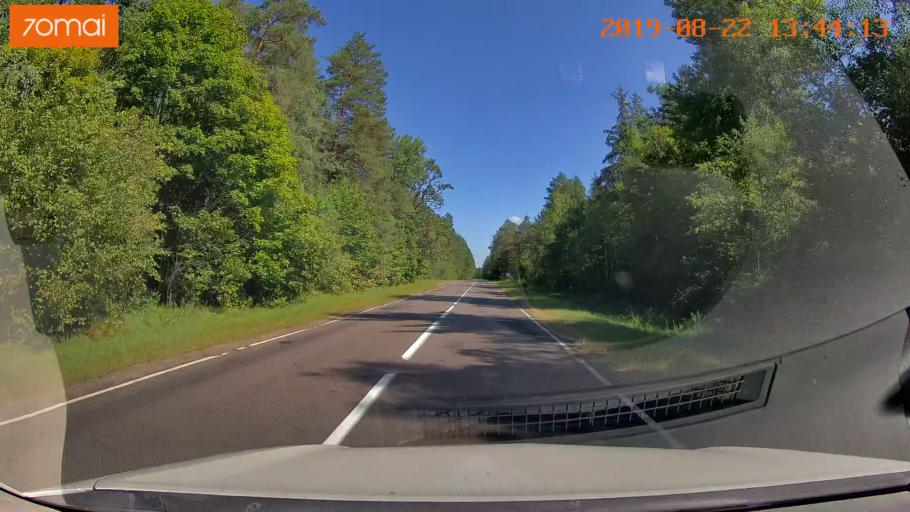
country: BY
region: Mogilev
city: Asipovichy
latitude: 53.2439
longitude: 28.4549
